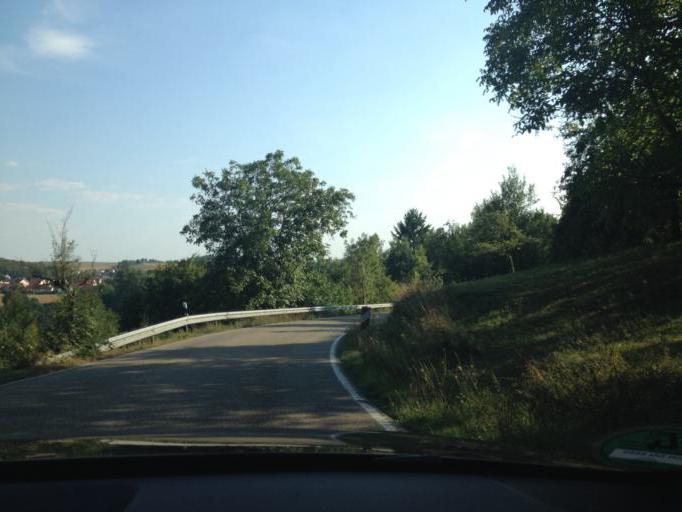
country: DE
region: Baden-Wuerttemberg
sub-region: Regierungsbezirk Stuttgart
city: Oedheim
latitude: 49.2767
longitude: 9.2239
